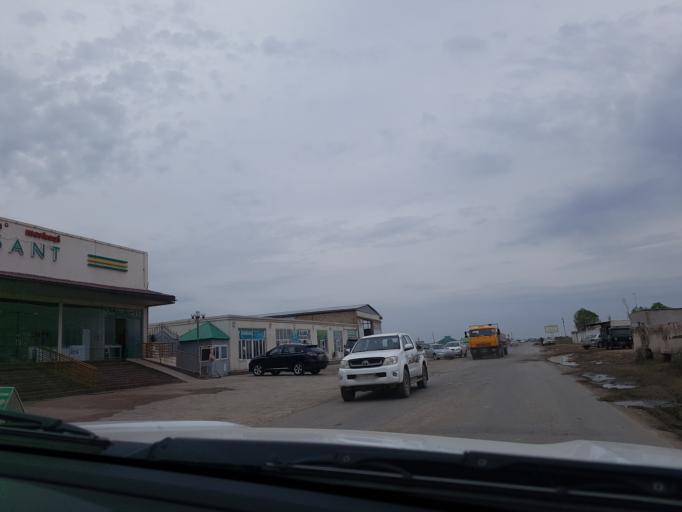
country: TM
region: Lebap
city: Turkmenabat
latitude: 39.0659
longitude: 63.5631
